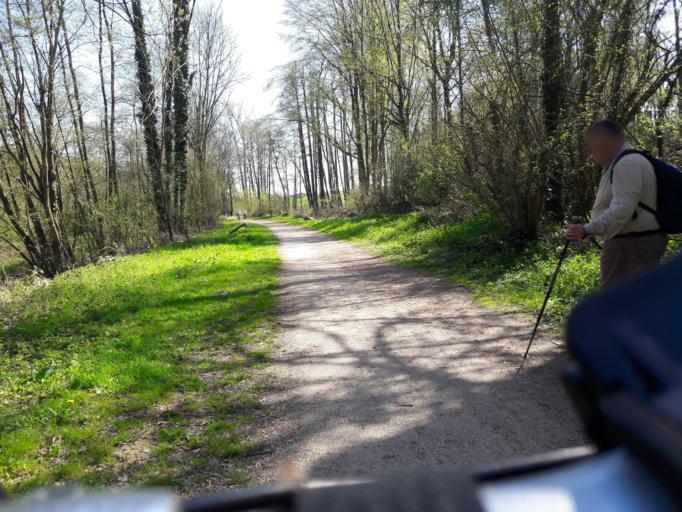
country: FR
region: Nord-Pas-de-Calais
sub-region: Departement du Nord
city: Ferriere-la-Grande
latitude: 50.2460
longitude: 4.0083
